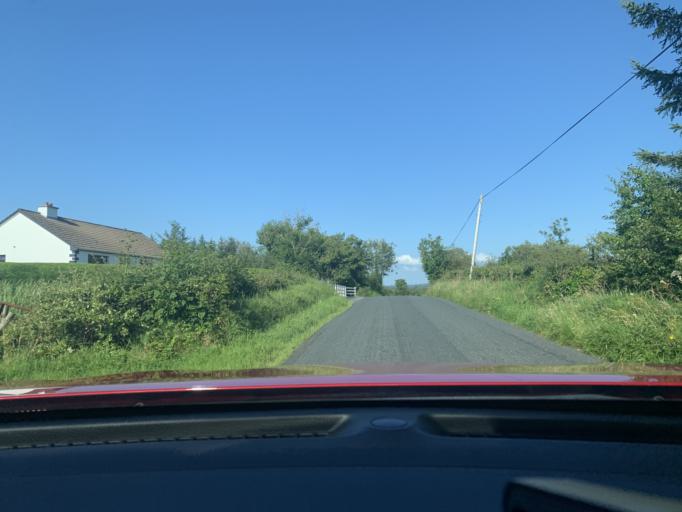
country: IE
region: Connaught
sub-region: Sligo
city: Tobercurry
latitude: 54.0913
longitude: -8.7964
